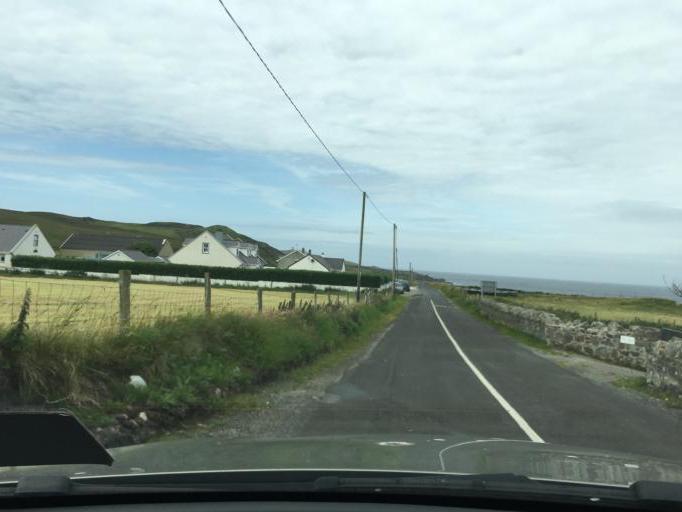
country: IE
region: Ulster
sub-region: County Donegal
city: Carndonagh
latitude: 55.3716
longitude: -7.3394
